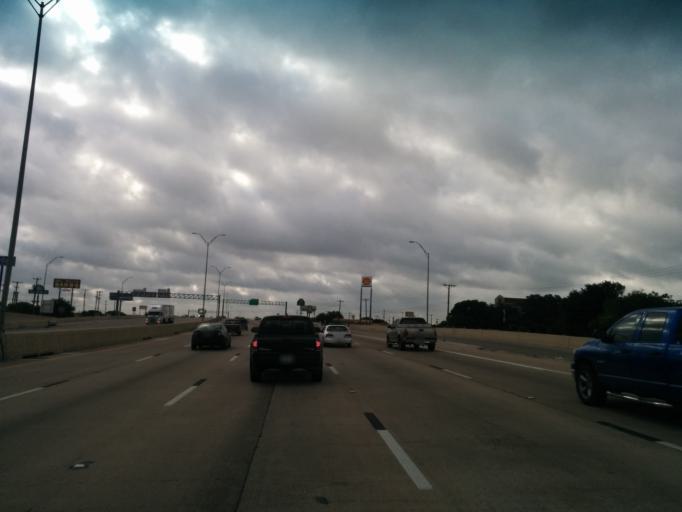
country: US
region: Texas
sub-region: Bexar County
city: Balcones Heights
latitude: 29.4846
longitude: -98.5385
